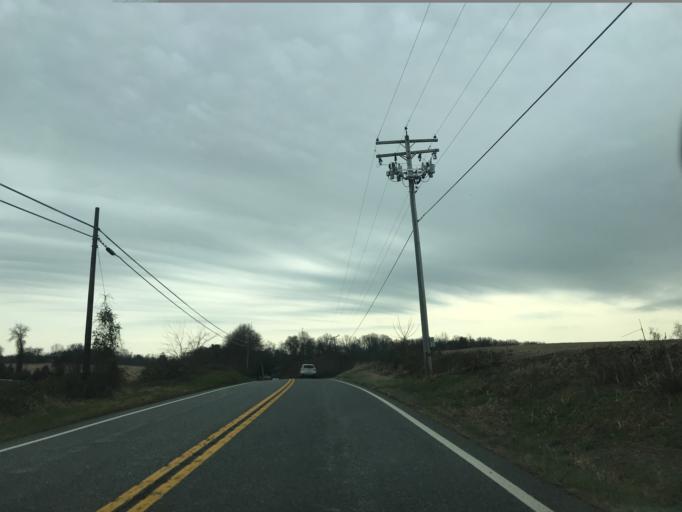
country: US
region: Maryland
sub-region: Harford County
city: Bel Air North
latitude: 39.5936
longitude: -76.3462
